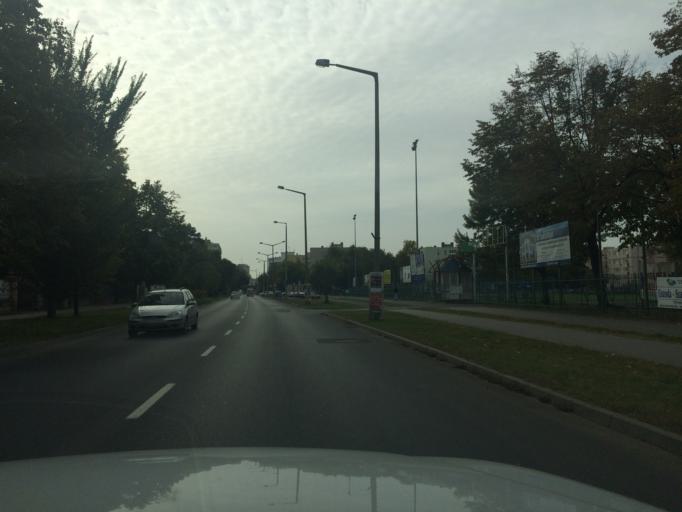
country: HU
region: Szabolcs-Szatmar-Bereg
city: Nyiregyhaza
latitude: 47.9699
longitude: 21.7153
